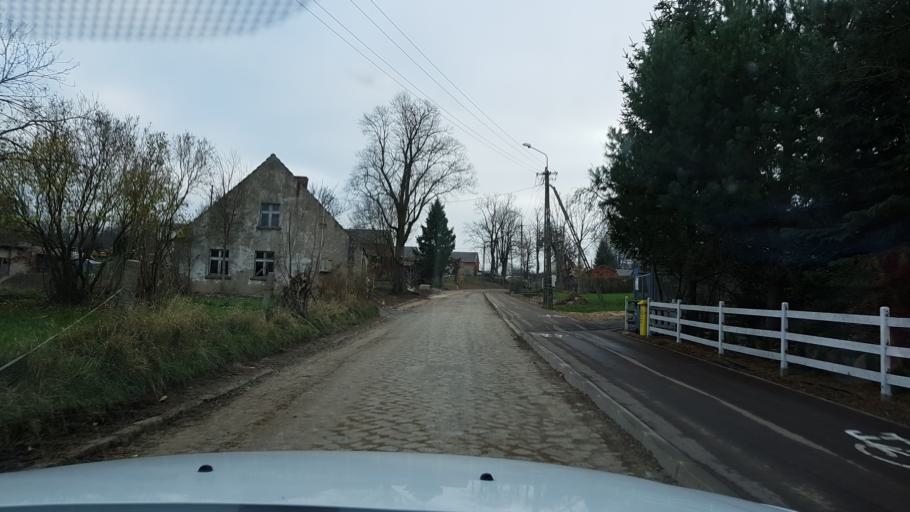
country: PL
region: West Pomeranian Voivodeship
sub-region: Powiat kolobrzeski
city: Grzybowo
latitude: 54.1213
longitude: 15.5221
